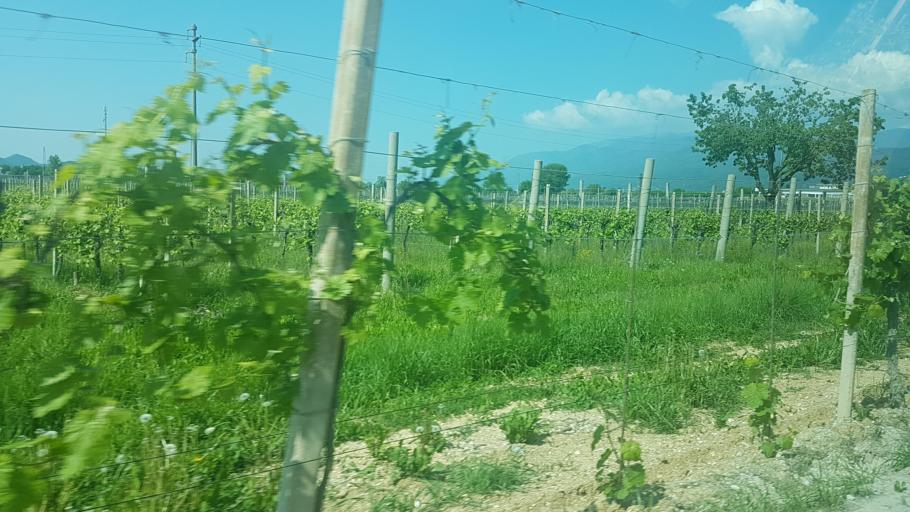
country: IT
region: Veneto
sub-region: Provincia di Treviso
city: Bigolino
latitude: 45.8775
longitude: 12.0141
